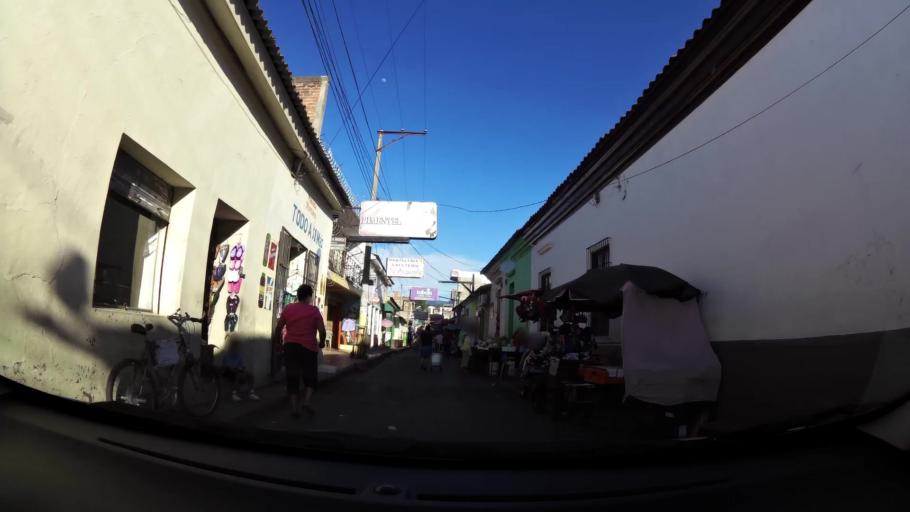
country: SV
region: Santa Ana
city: Metapan
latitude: 14.3311
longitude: -89.4465
